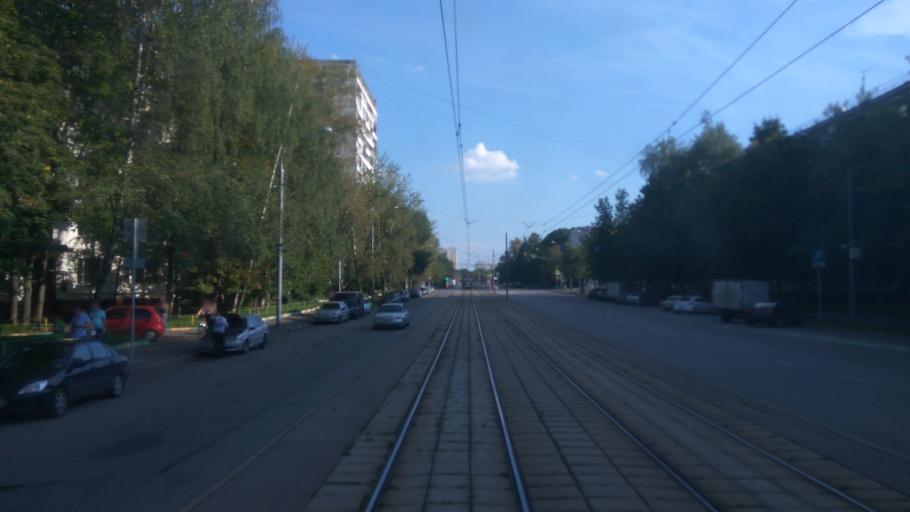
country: RU
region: Moscow
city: Perovo
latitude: 55.7577
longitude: 37.7885
